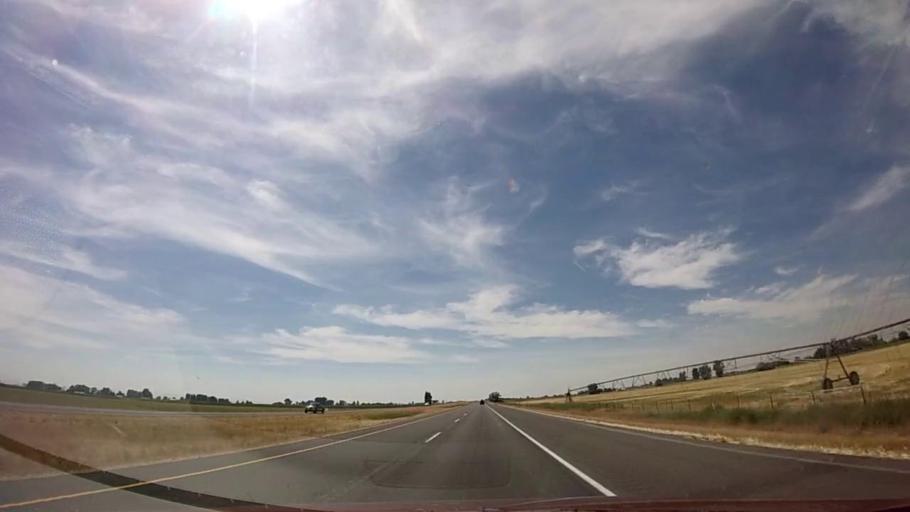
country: US
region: Idaho
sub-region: Minidoka County
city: Rupert
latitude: 42.5690
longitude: -113.6537
